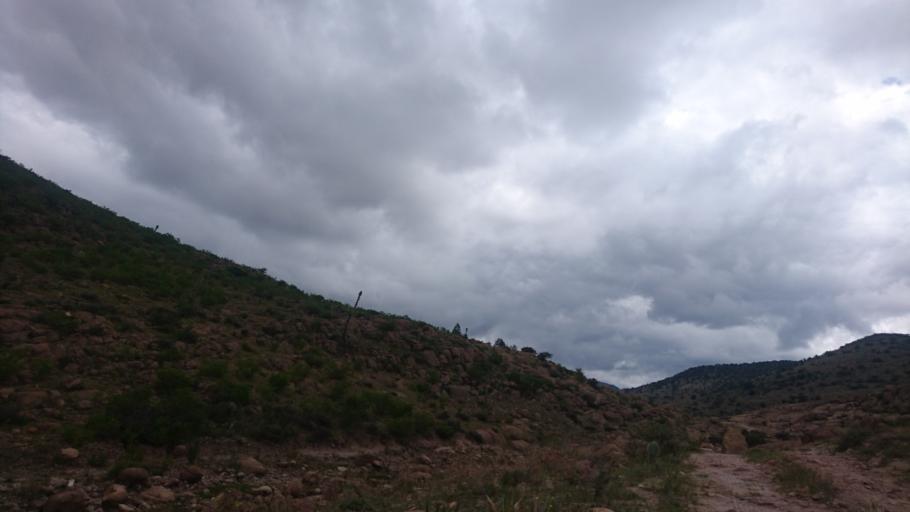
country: MX
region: San Luis Potosi
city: Escalerillas
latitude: 22.0745
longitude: -101.0940
